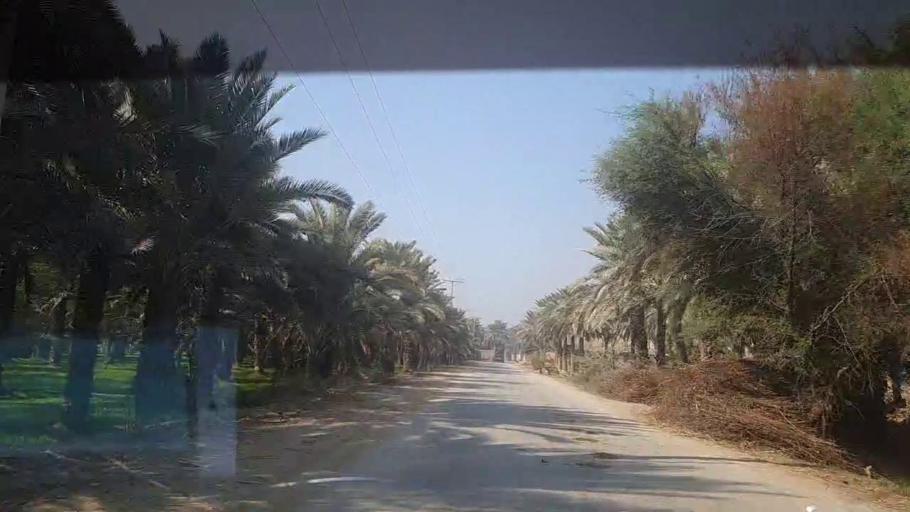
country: PK
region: Sindh
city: Kot Diji
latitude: 27.3773
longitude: 68.6929
